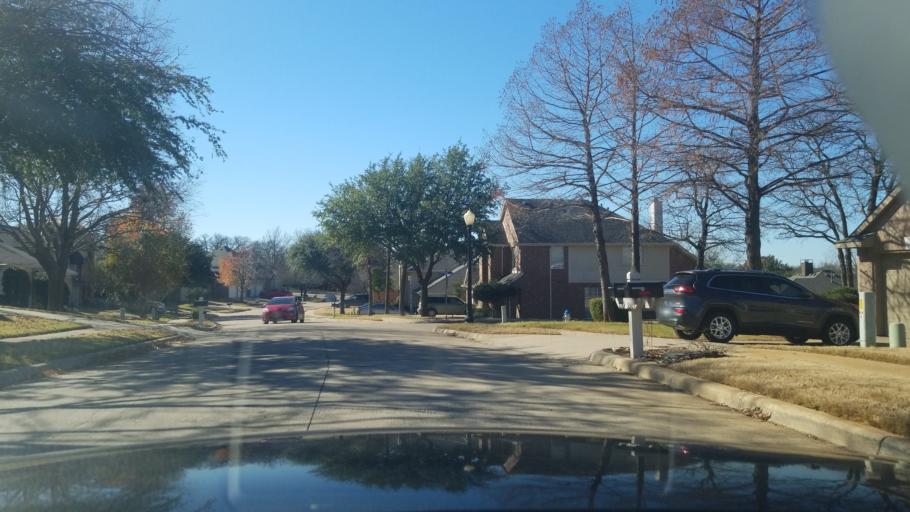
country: US
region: Texas
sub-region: Denton County
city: Corinth
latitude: 33.1579
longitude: -97.0757
